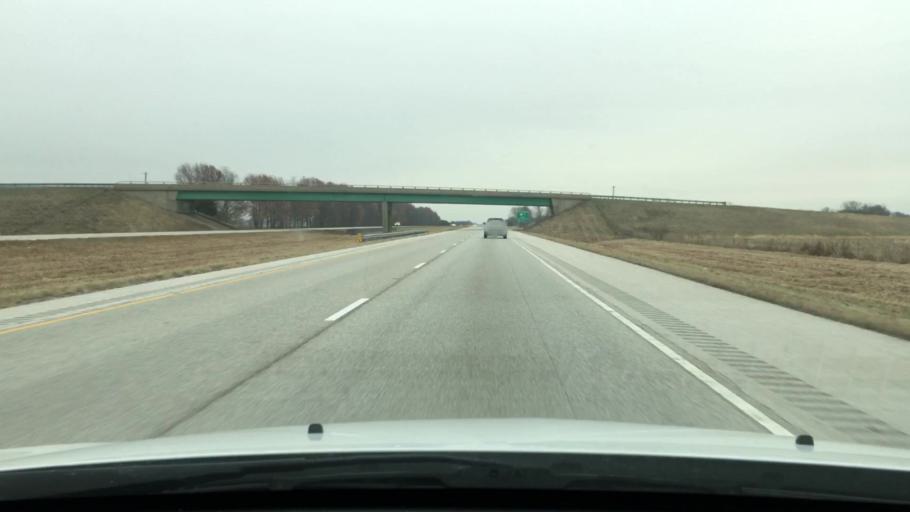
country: US
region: Illinois
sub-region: Morgan County
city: South Jacksonville
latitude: 39.6802
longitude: -90.3277
